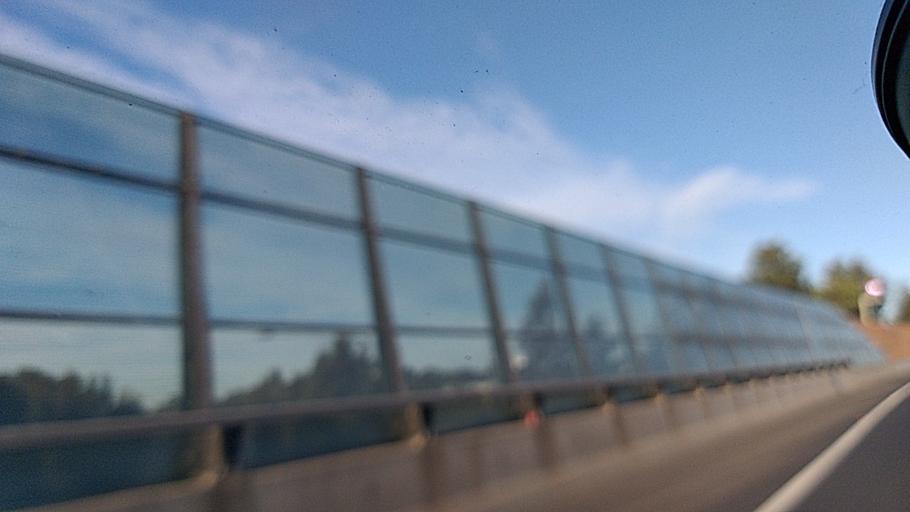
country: AU
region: New South Wales
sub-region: Liverpool
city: Miller
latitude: -33.9265
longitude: 150.8643
